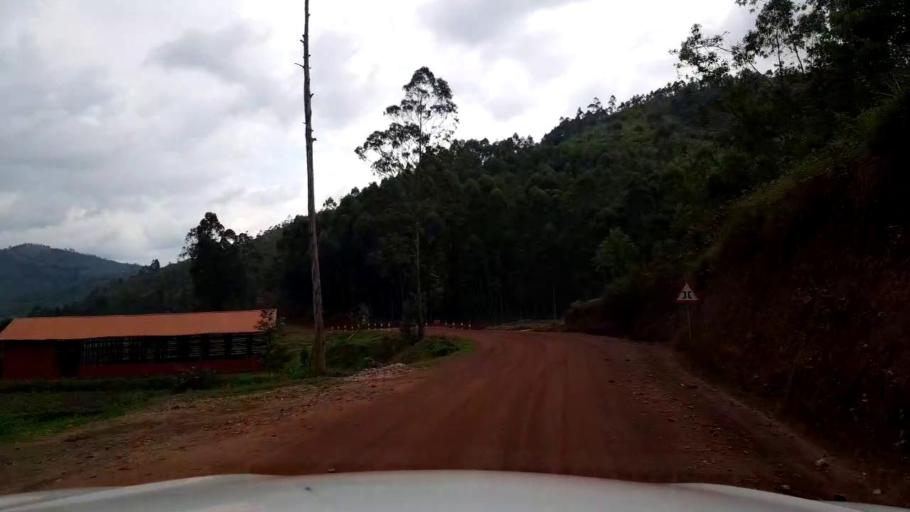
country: RW
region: Northern Province
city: Musanze
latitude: -1.6729
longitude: 29.7991
